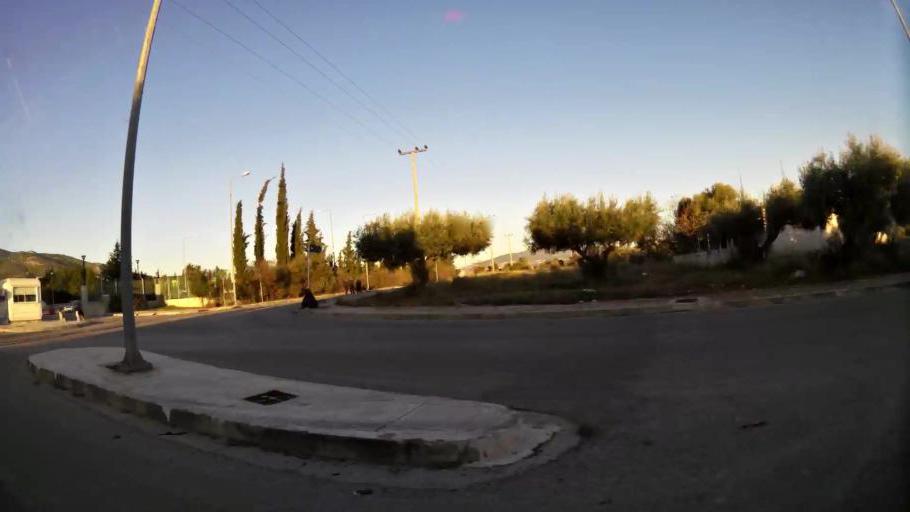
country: GR
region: Attica
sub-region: Nomarchia Dytikis Attikis
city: Ano Liosia
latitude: 38.0803
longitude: 23.6868
